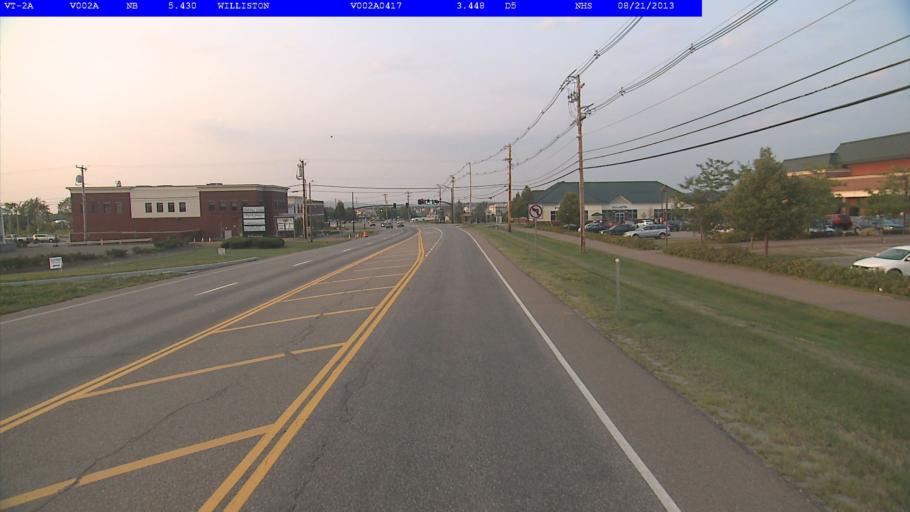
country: US
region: Vermont
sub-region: Chittenden County
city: Williston
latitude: 44.4457
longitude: -73.1116
